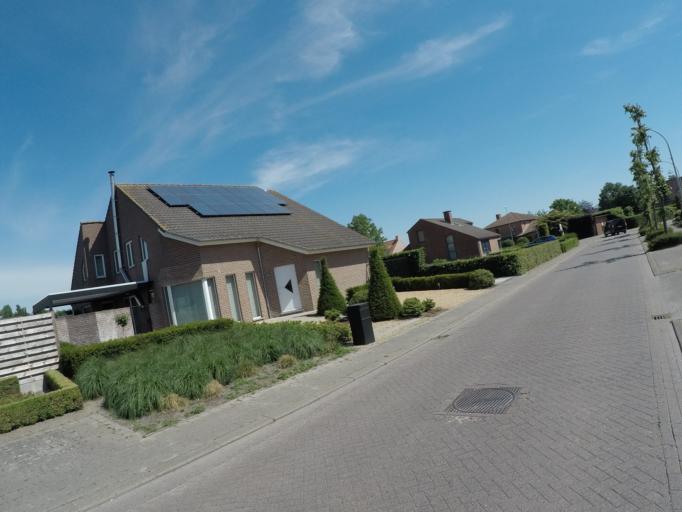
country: BE
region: Flanders
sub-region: Provincie Antwerpen
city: Wuustwezel
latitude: 51.4034
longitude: 4.6439
